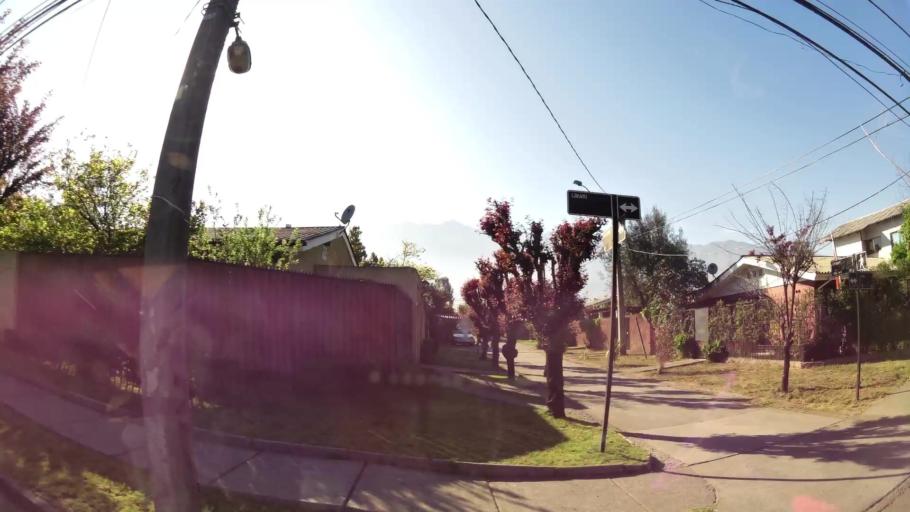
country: CL
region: Santiago Metropolitan
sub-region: Provincia de Santiago
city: Villa Presidente Frei, Nunoa, Santiago, Chile
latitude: -33.4584
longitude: -70.5515
